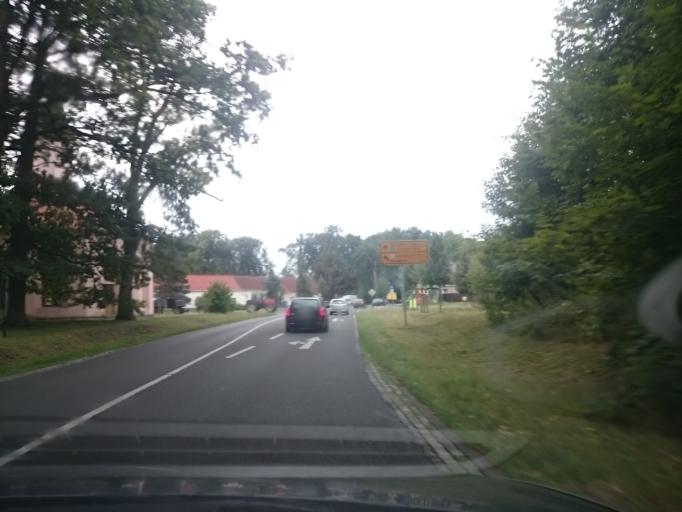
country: DE
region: Brandenburg
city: Gransee
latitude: 53.0802
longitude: 13.1852
